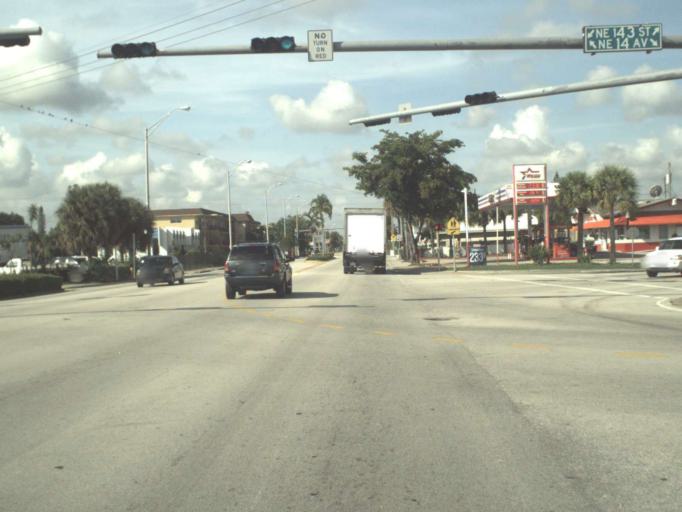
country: US
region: Florida
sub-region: Miami-Dade County
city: North Miami
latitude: 25.9075
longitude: -80.1711
